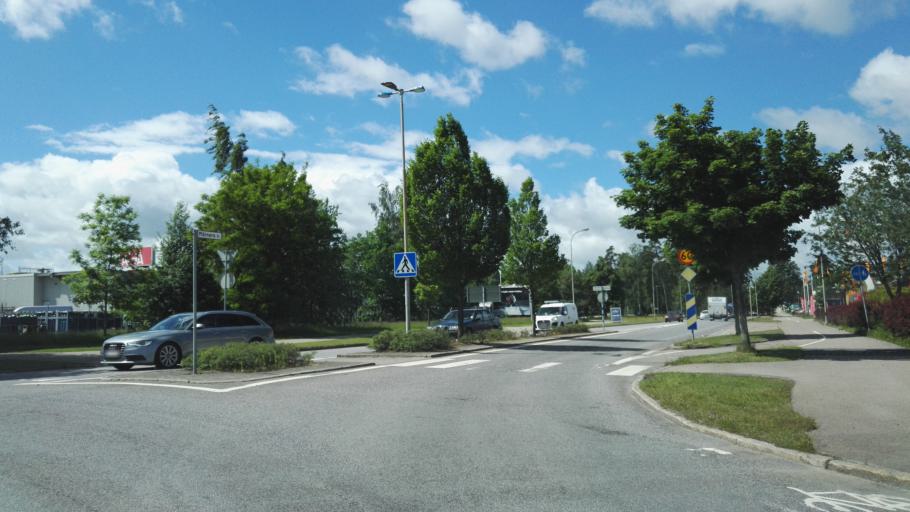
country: SE
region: Kronoberg
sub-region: Vaxjo Kommun
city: Vaexjoe
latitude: 56.8883
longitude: 14.7823
